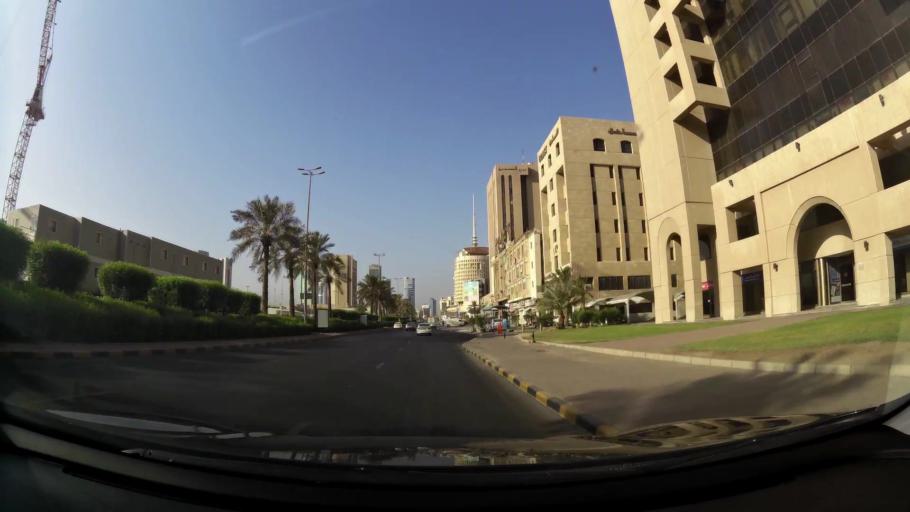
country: KW
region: Al Asimah
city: Kuwait City
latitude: 29.3746
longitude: 47.9859
